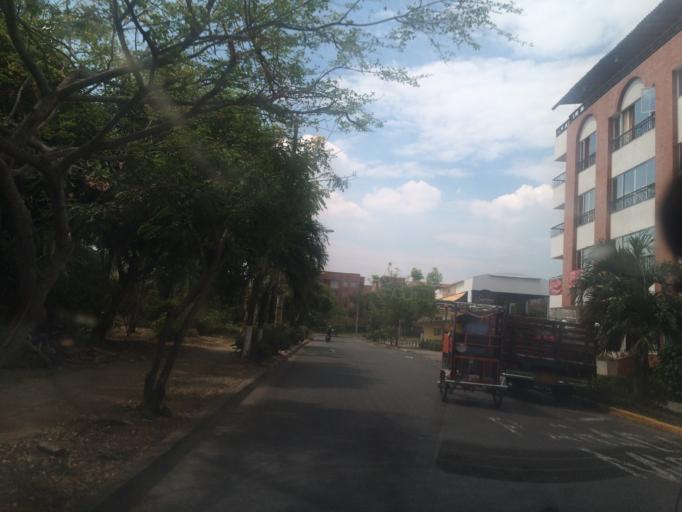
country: CO
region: Valle del Cauca
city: Cali
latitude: 3.3766
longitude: -76.5201
